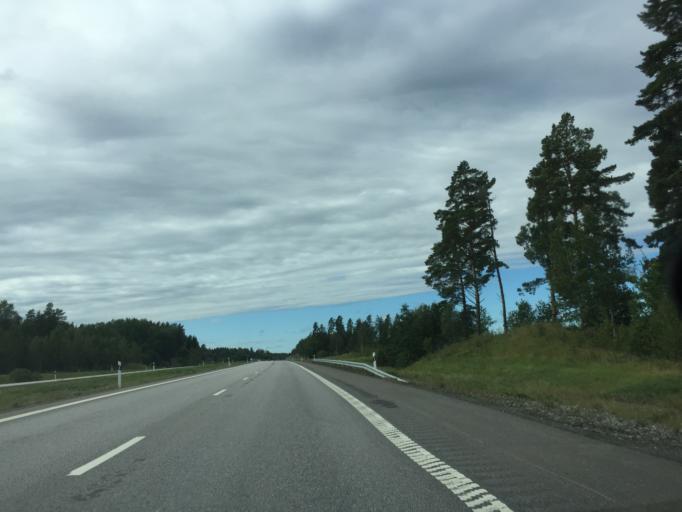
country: SE
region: Vaestmanland
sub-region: Arboga Kommun
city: Arboga
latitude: 59.4247
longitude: 15.8237
